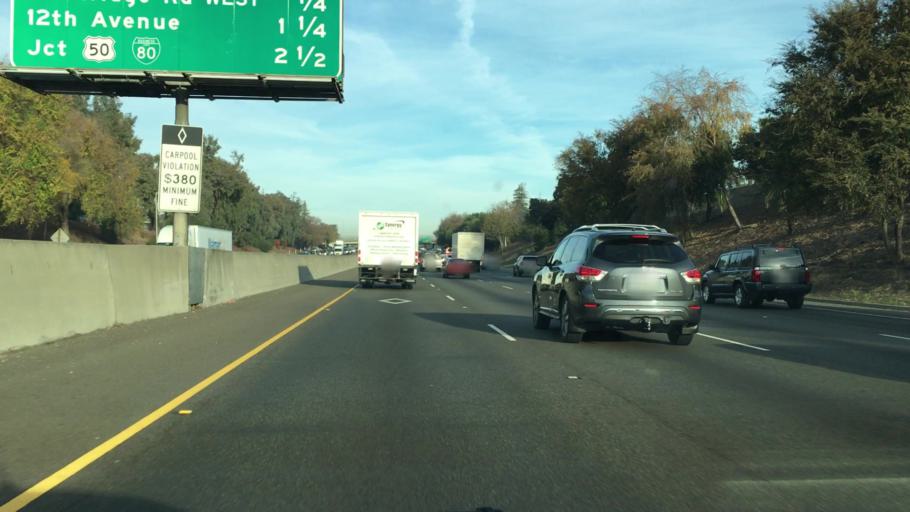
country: US
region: California
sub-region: Sacramento County
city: Parkway
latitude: 38.5208
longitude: -121.4654
